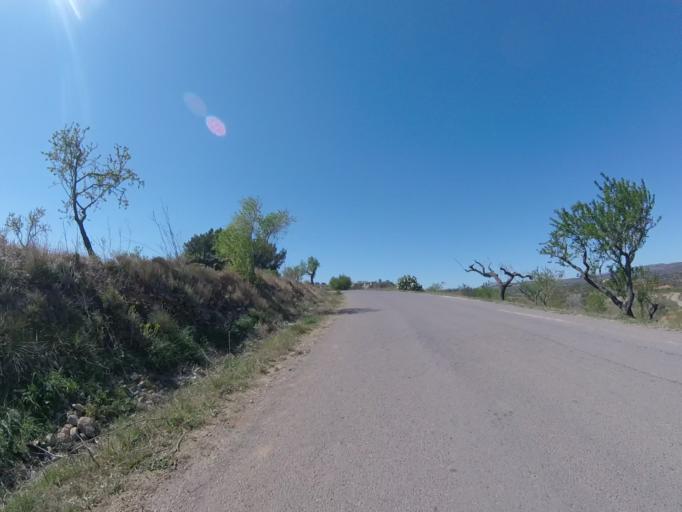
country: ES
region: Valencia
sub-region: Provincia de Castello
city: Cuevas de Vinroma
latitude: 40.3800
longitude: 0.1382
